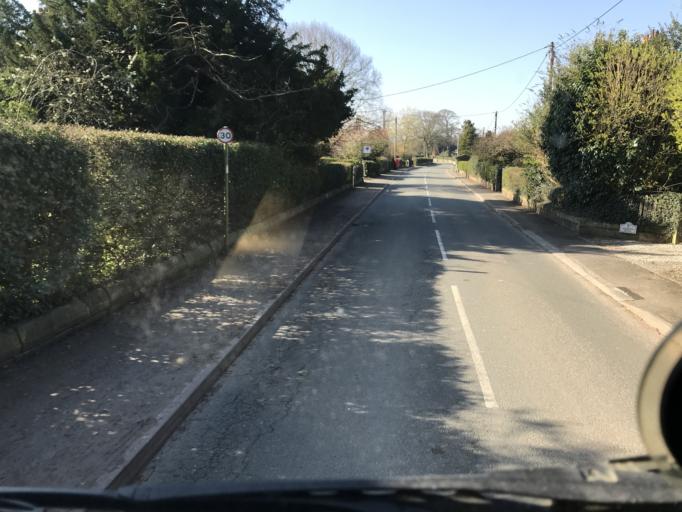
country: GB
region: England
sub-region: Cheshire West and Chester
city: Waverton
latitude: 53.1541
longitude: -2.8310
